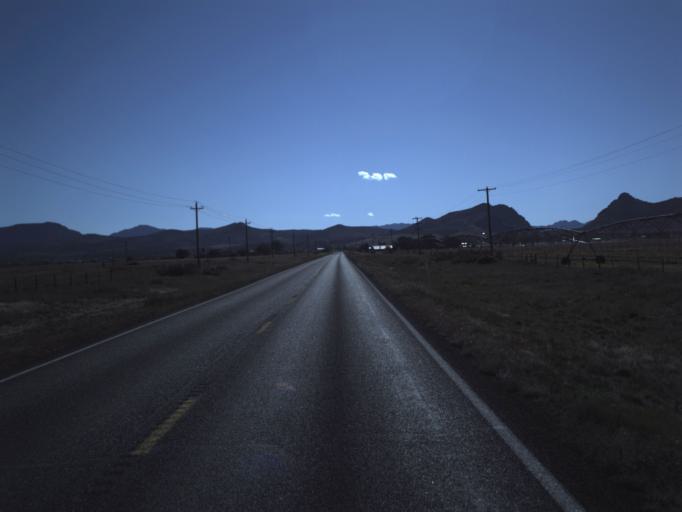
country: US
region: Utah
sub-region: Washington County
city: Enterprise
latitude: 37.6785
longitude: -113.5702
